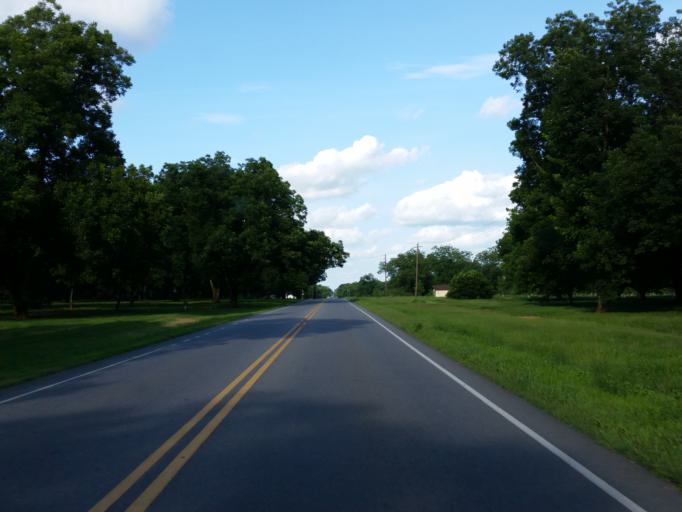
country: US
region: Georgia
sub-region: Crisp County
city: Cordele
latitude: 31.9618
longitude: -83.9519
